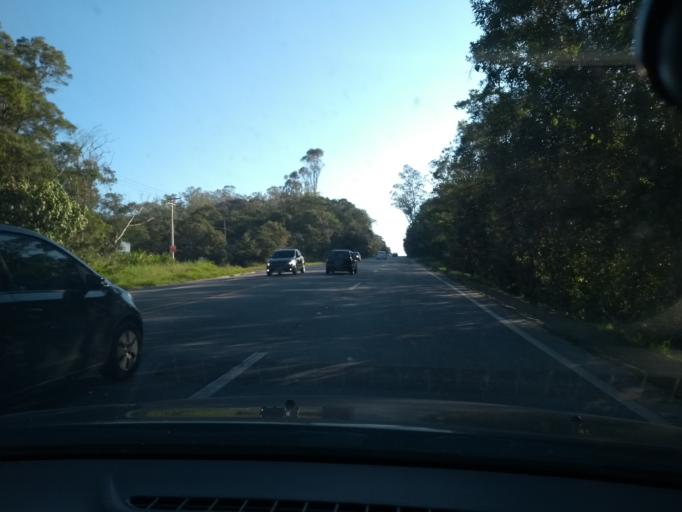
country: BR
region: Sao Paulo
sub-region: Rio Grande Da Serra
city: Rio Grande da Serra
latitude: -23.7785
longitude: -46.4842
